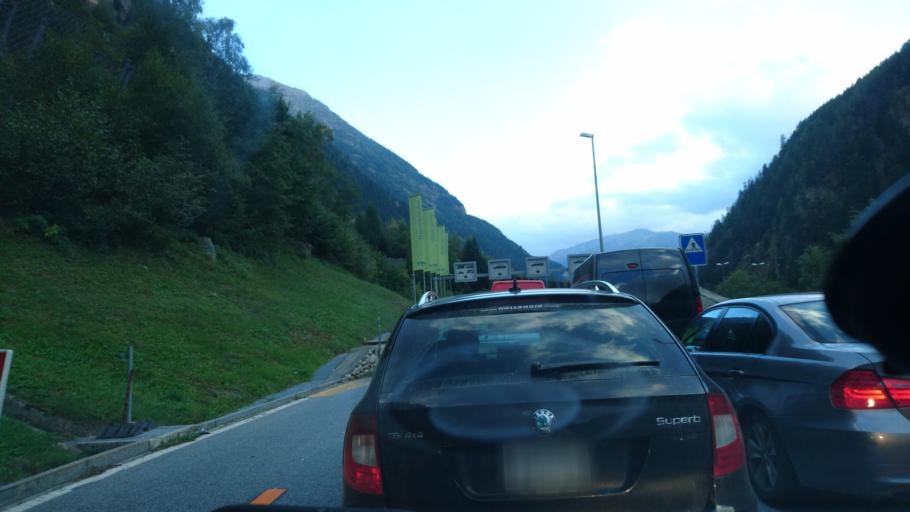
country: CH
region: Valais
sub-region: Leuk District
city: Gampel
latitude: 46.3643
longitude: 7.7578
